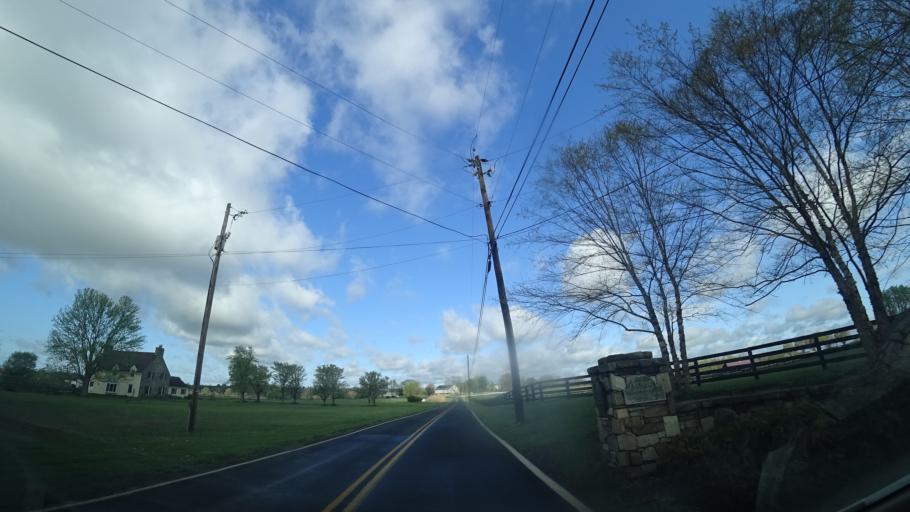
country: US
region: Virginia
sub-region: Loudoun County
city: Lowes Island
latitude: 39.1056
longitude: -77.3767
